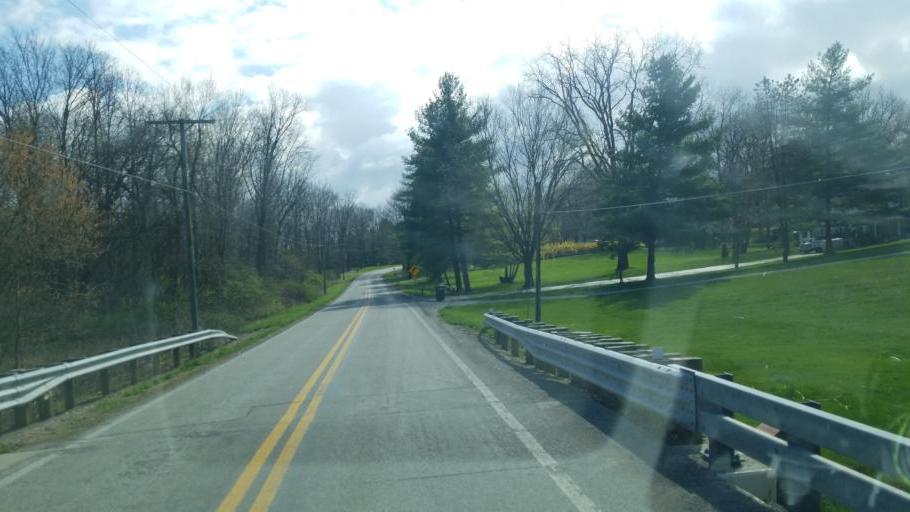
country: US
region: Ohio
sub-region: Delaware County
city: Delaware
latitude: 40.3660
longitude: -83.0290
